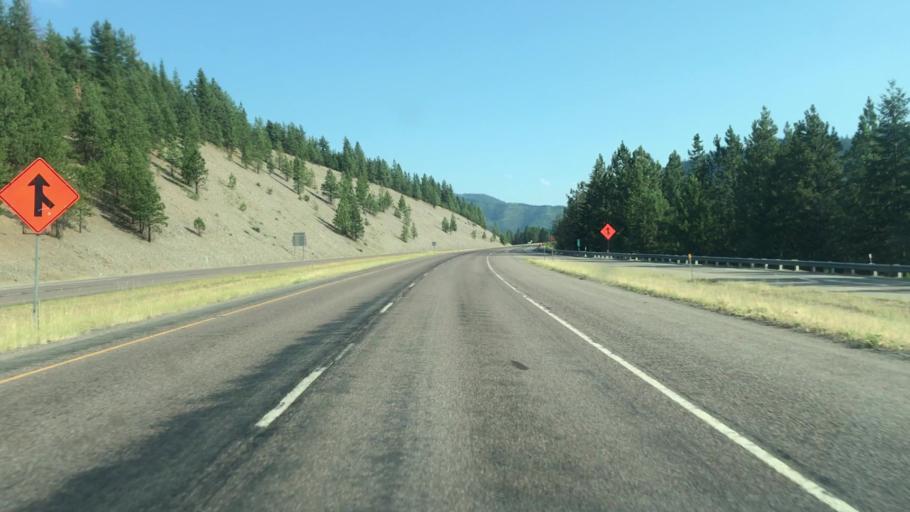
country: US
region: Montana
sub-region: Mineral County
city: Superior
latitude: 47.0238
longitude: -114.7380
